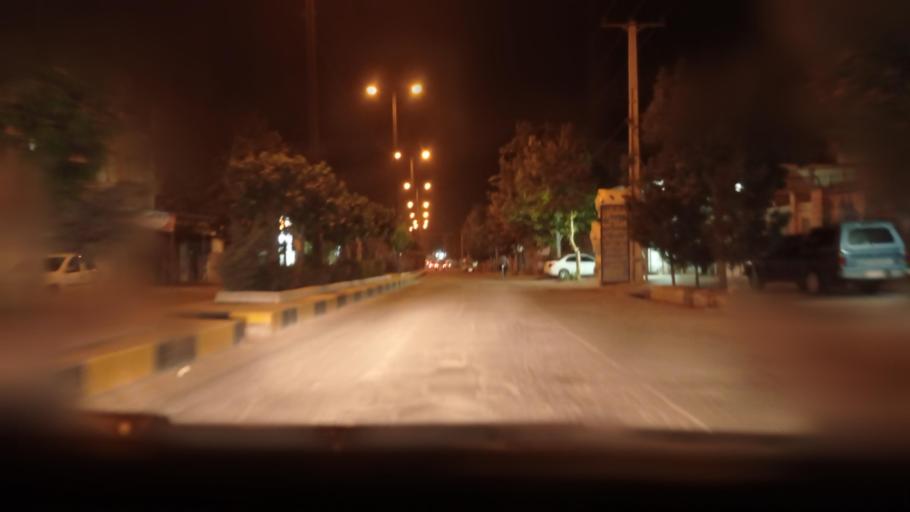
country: IR
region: Lorestan
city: Kuhdasht
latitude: 33.5389
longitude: 47.6094
